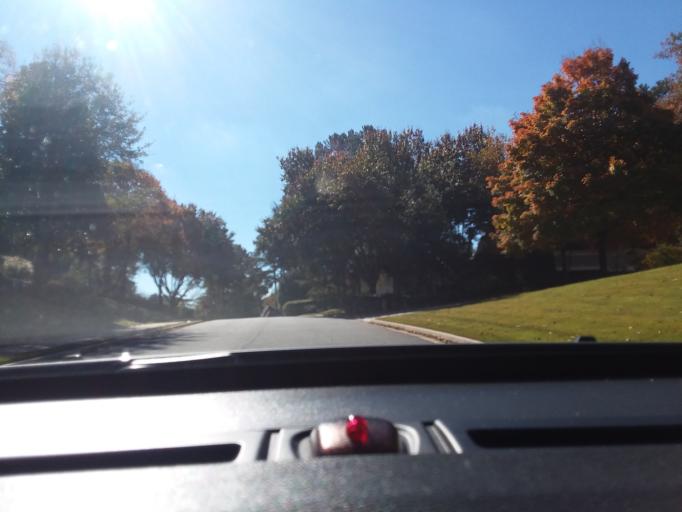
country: US
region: Georgia
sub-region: Fulton County
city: Johns Creek
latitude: 34.0339
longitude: -84.1755
